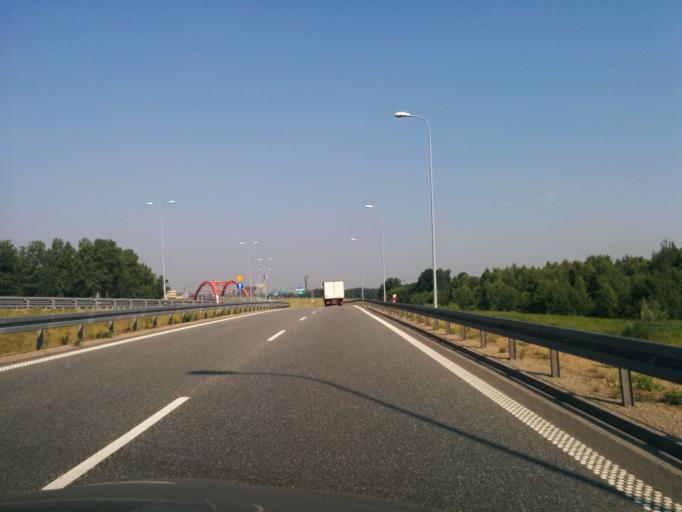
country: PL
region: Silesian Voivodeship
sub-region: Powiat gliwicki
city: Przyszowice
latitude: 50.2664
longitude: 18.7369
